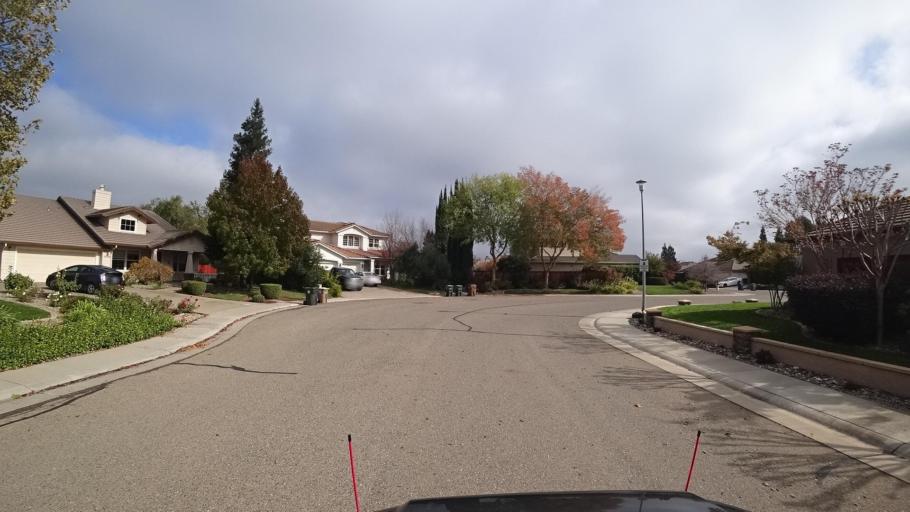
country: US
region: California
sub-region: Sacramento County
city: Elk Grove
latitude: 38.4265
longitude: -121.3652
